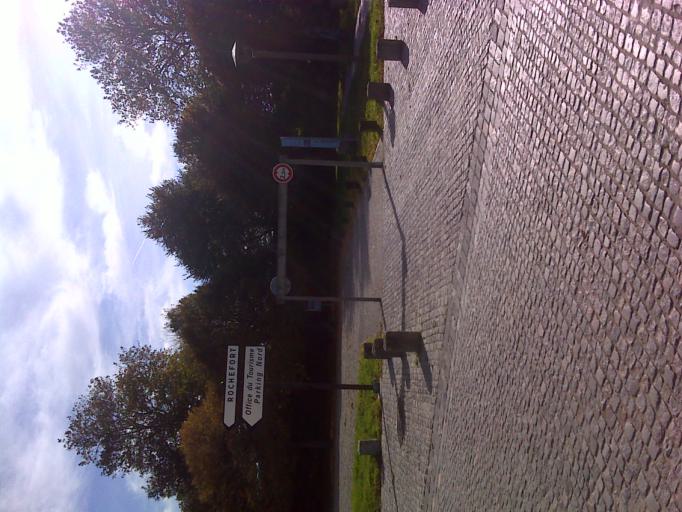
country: FR
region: Poitou-Charentes
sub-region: Departement de la Charente-Maritime
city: Marennes
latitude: 45.8651
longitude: -1.0713
